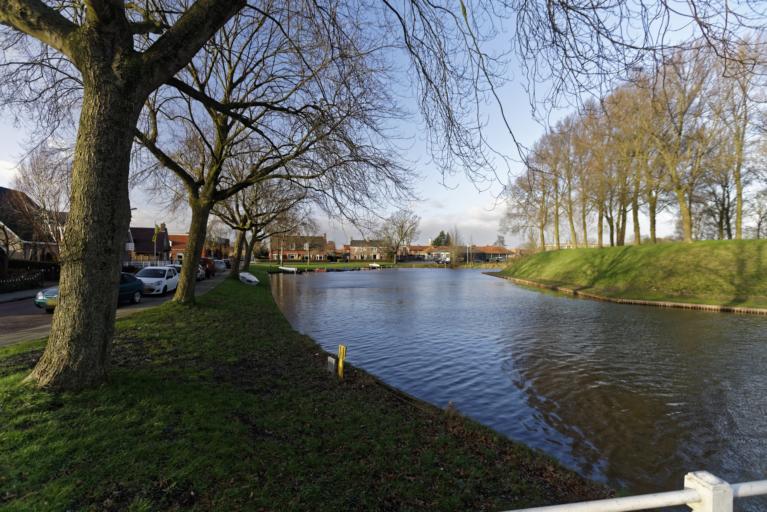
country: NL
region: Friesland
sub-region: Gemeente Dongeradeel
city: Dokkum
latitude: 53.3267
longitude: 5.9943
